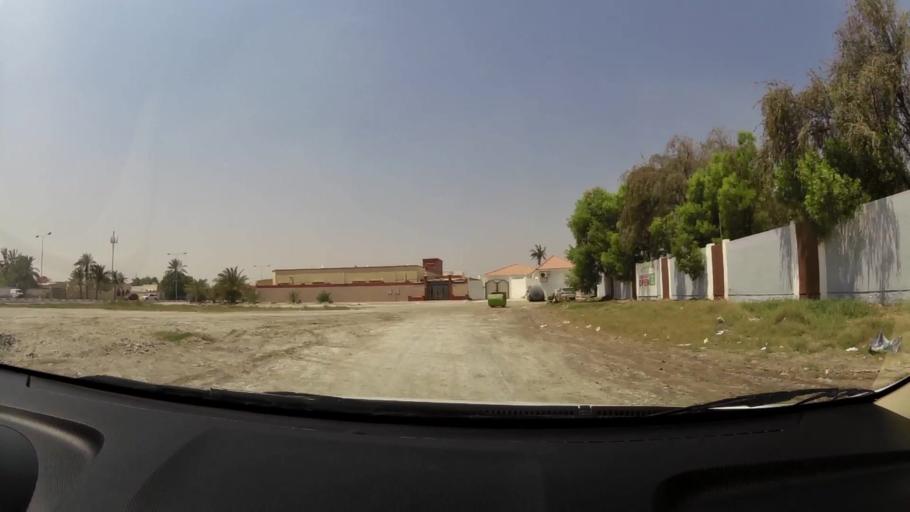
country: AE
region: Umm al Qaywayn
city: Umm al Qaywayn
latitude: 25.5564
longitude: 55.5552
